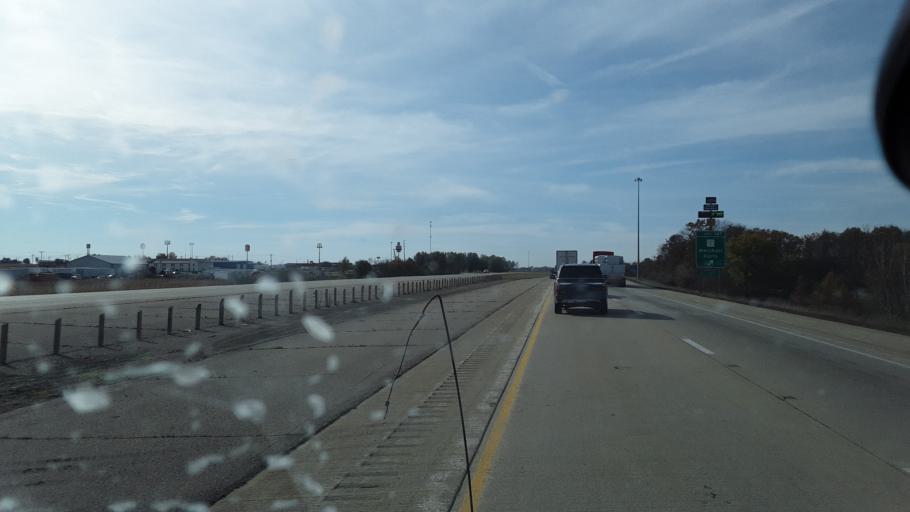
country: US
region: Illinois
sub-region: Clark County
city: Marshall
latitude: 39.4227
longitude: -87.6848
